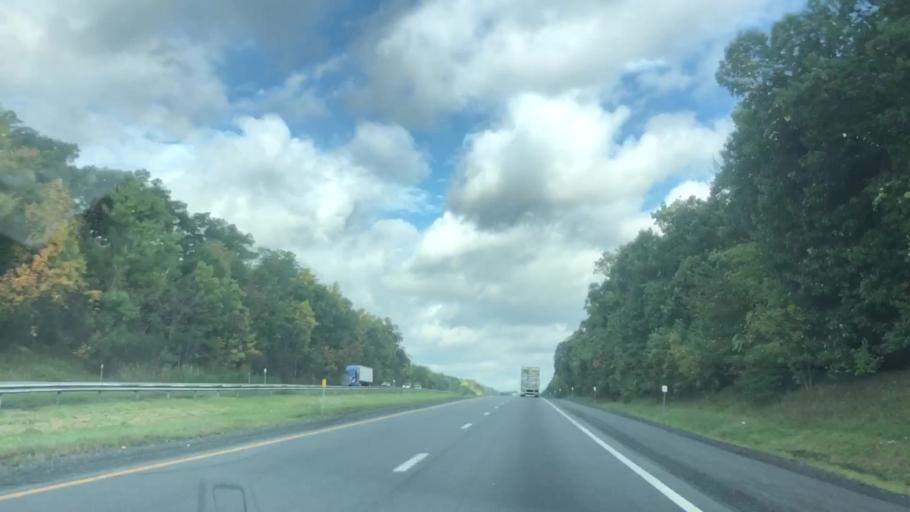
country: US
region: New York
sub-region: Orange County
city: Vails Gate
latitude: 41.4612
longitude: -74.0673
